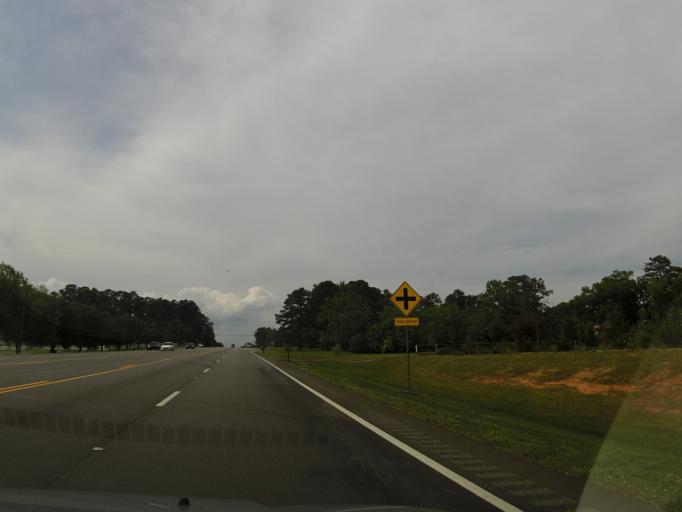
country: US
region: Georgia
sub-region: McDuffie County
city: Thomson
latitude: 33.5382
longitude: -82.5076
